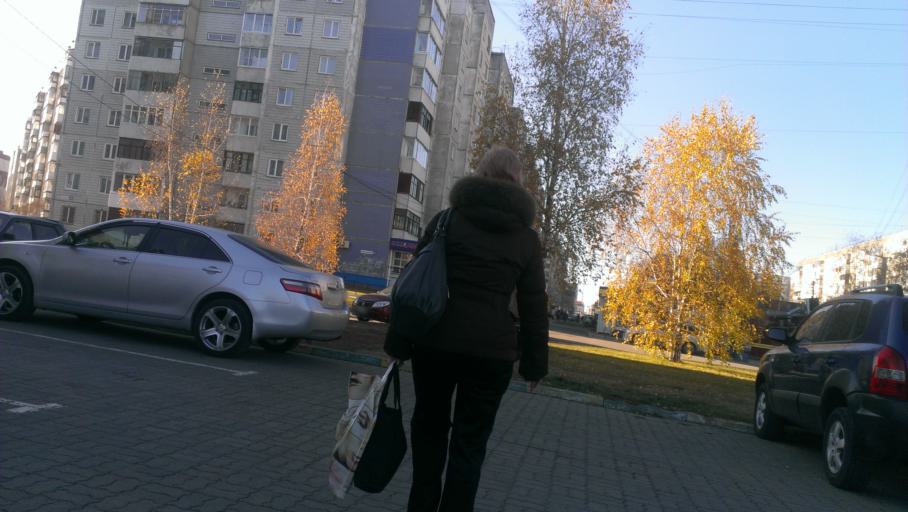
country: RU
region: Altai Krai
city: Novosilikatnyy
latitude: 53.3351
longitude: 83.6763
